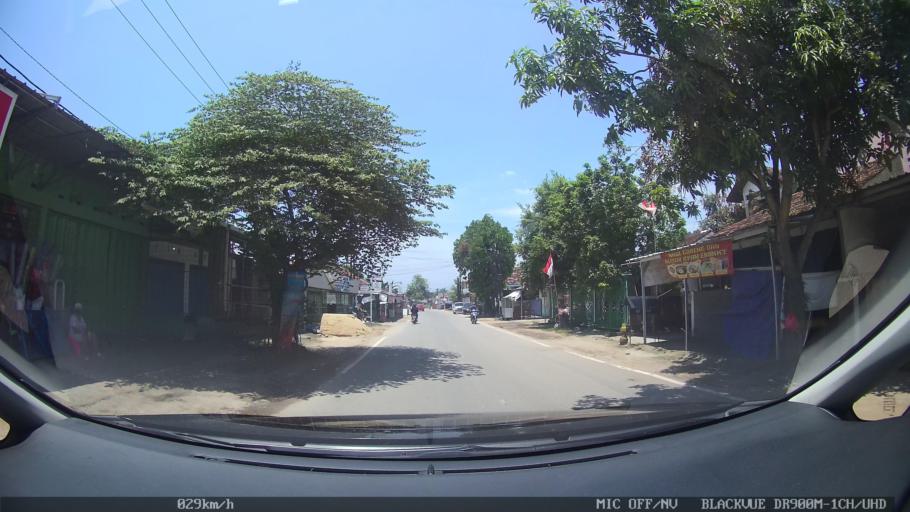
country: ID
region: Lampung
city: Kedaton
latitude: -5.3770
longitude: 105.2892
